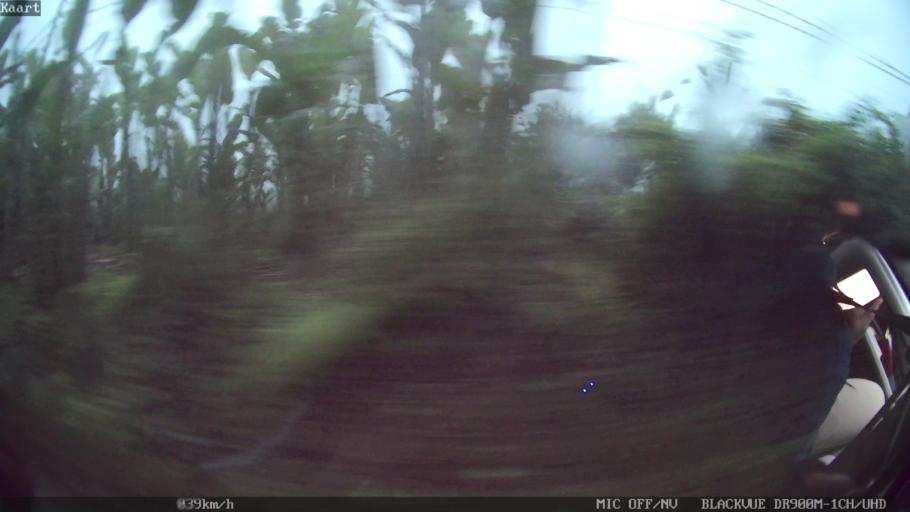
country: ID
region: Bali
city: Banjar Taro Kelod
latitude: -8.3451
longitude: 115.2797
